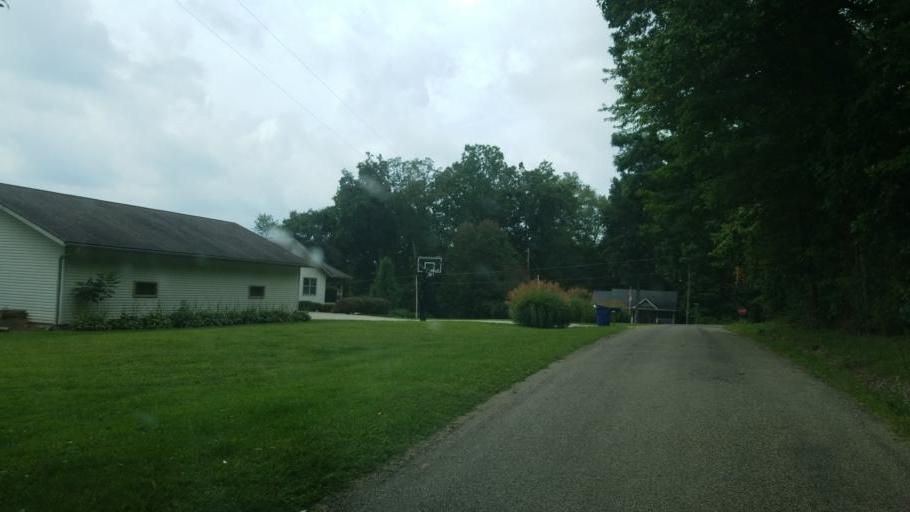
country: US
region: Ohio
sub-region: Knox County
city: Danville
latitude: 40.4559
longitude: -82.3260
